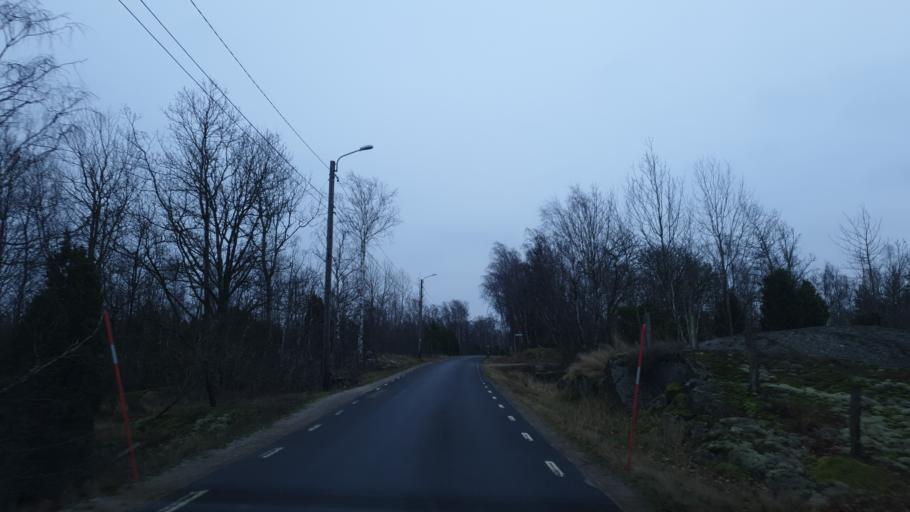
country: SE
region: Blekinge
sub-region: Karlskrona Kommun
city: Karlskrona
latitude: 56.1099
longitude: 15.6220
